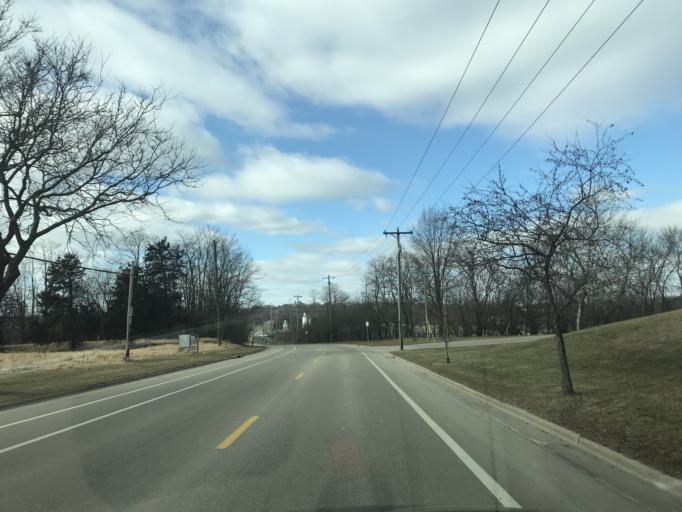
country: US
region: Wisconsin
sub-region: Dane County
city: Monona
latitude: 43.1141
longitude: -89.3045
